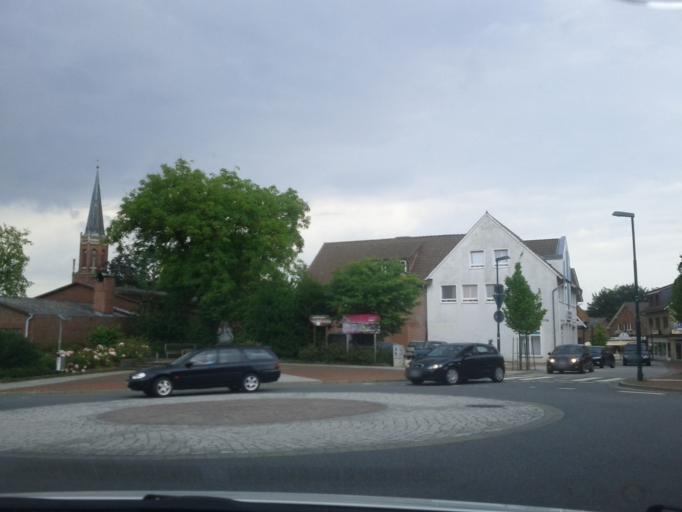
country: DE
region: Lower Saxony
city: Harsefeld
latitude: 53.4522
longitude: 9.5005
